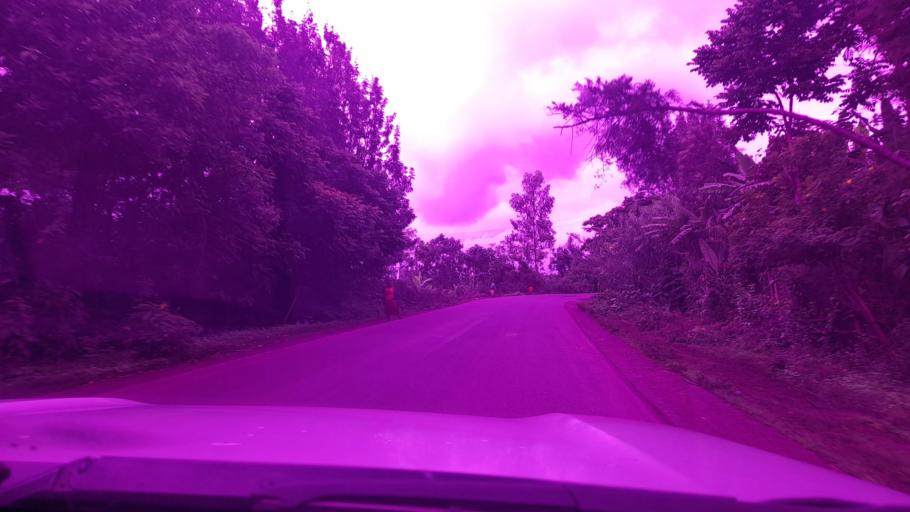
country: ET
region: Oromiya
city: Jima
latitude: 7.9216
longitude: 37.4087
